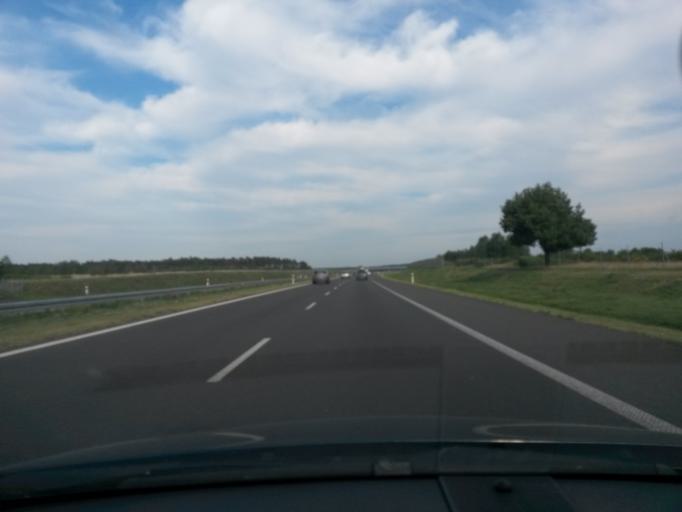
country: PL
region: Greater Poland Voivodeship
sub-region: Powiat turecki
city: Wladyslawow
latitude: 52.1522
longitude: 18.4761
